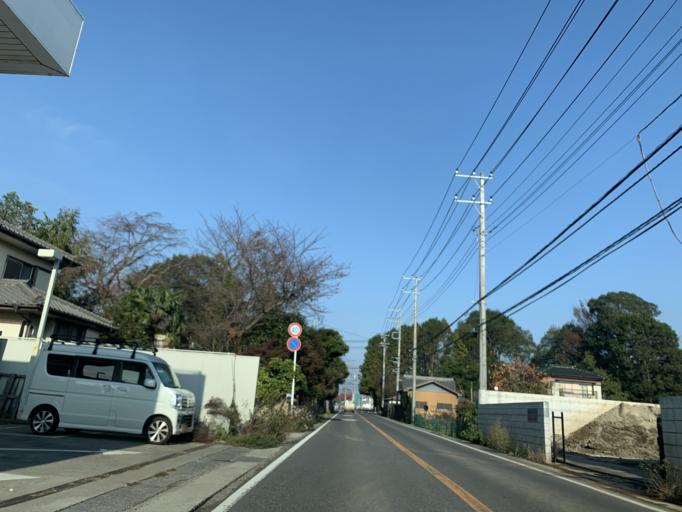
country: JP
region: Chiba
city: Nagareyama
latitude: 35.8618
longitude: 139.9223
